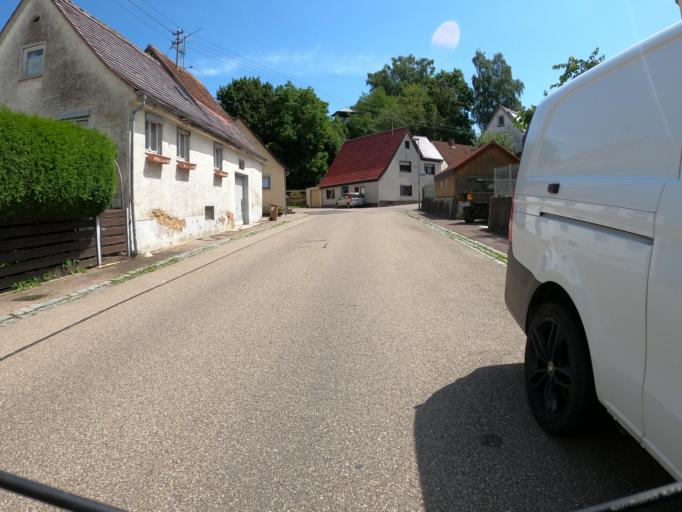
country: DE
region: Bavaria
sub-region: Swabia
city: Leipheim
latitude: 48.4450
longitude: 10.2218
